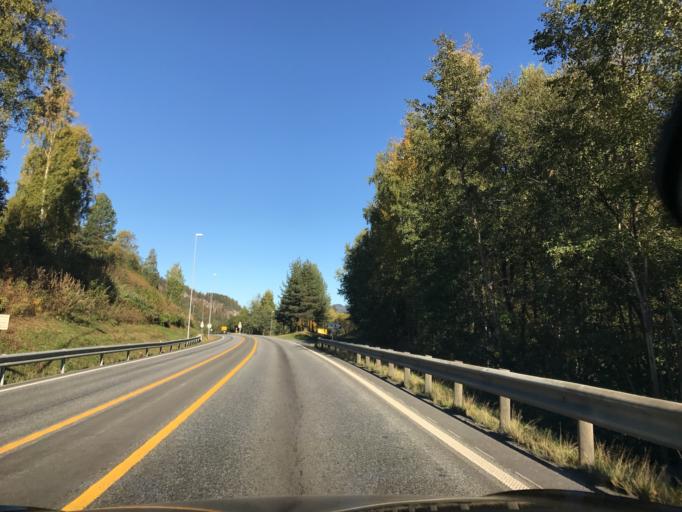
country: NO
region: Hedmark
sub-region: Ringsaker
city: Moelv
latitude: 60.9323
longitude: 10.6537
